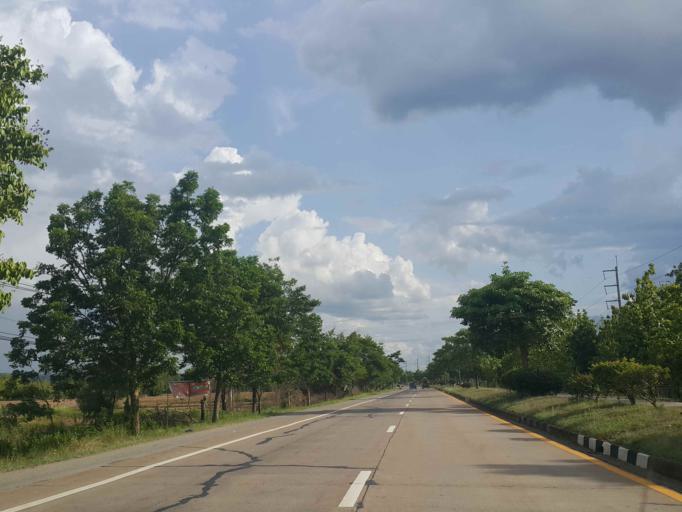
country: TH
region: Phrae
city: Sung Men
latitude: 18.0156
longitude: 100.1076
